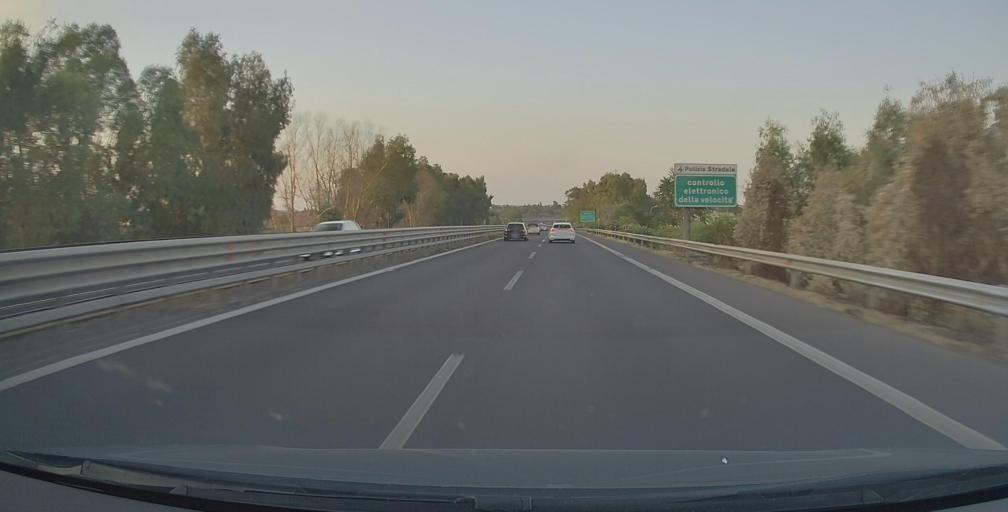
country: IT
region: Sicily
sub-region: Catania
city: San Gregorio di Catania
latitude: 37.5699
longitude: 15.1057
